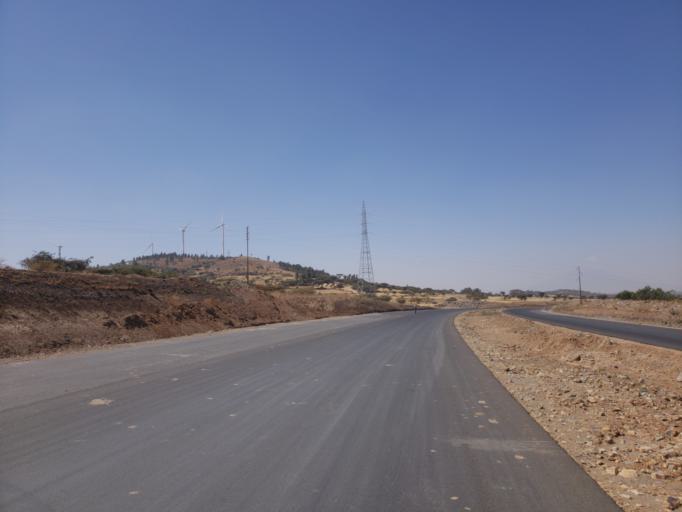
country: ET
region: Oromiya
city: Mojo
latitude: 8.5653
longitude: 39.1613
